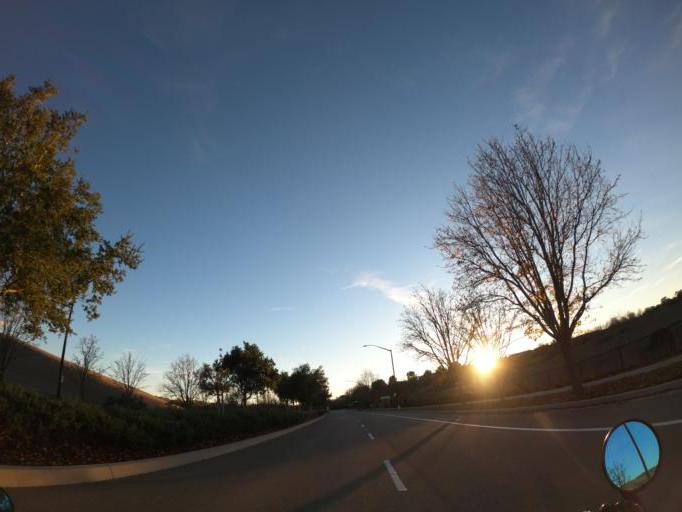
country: US
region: California
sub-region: Contra Costa County
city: Blackhawk
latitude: 37.7556
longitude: -121.8883
